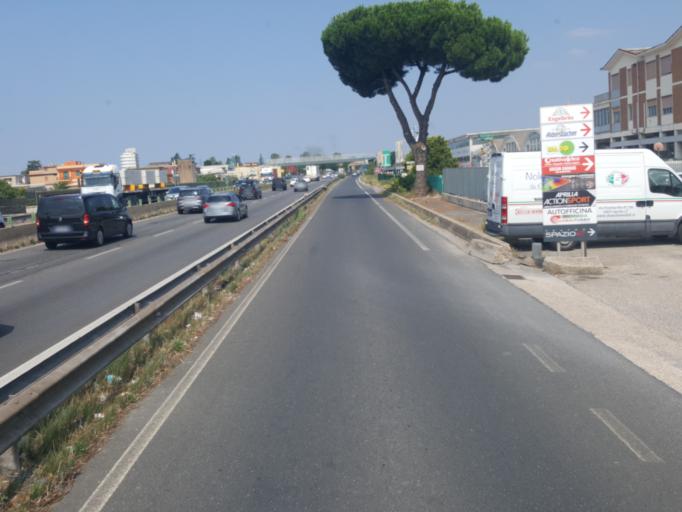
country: IT
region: Latium
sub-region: Provincia di Latina
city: Aprilia
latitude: 41.5756
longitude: 12.6578
